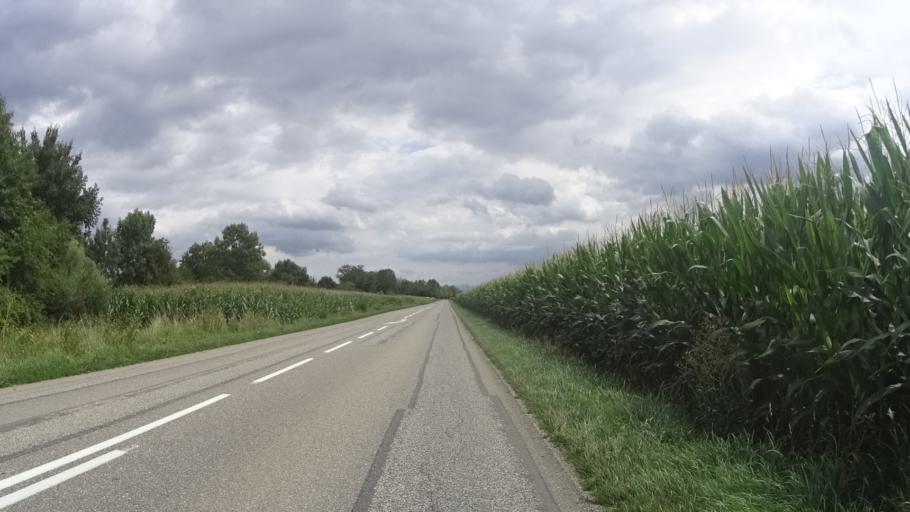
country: FR
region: Alsace
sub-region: Departement du Bas-Rhin
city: Weyersheim
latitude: 48.7081
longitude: 7.8246
